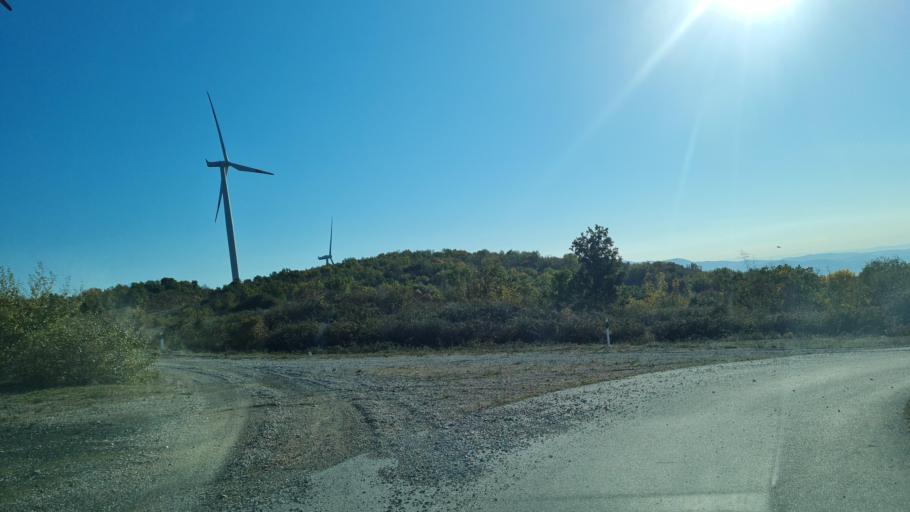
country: MK
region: Bogdanci
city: Bogdanci
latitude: 41.2302
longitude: 22.5623
